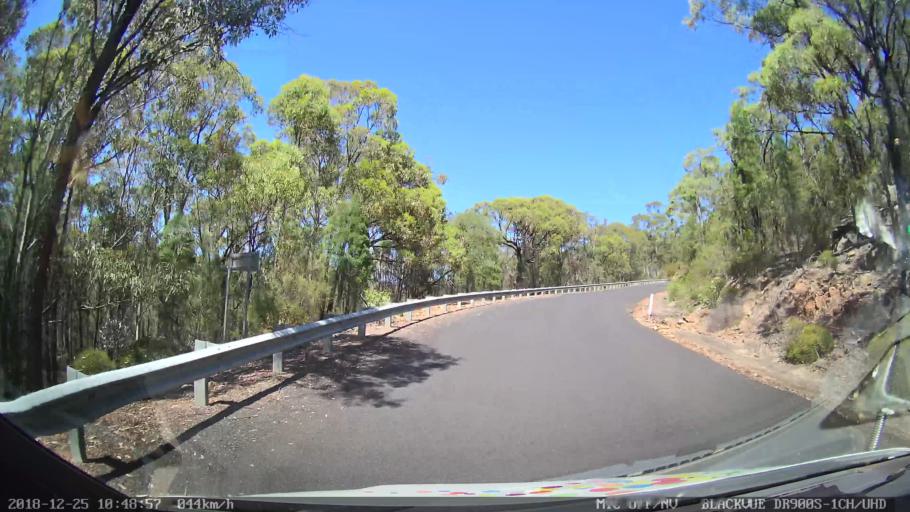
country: AU
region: New South Wales
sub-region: Upper Hunter Shire
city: Merriwa
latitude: -32.4490
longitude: 150.2724
